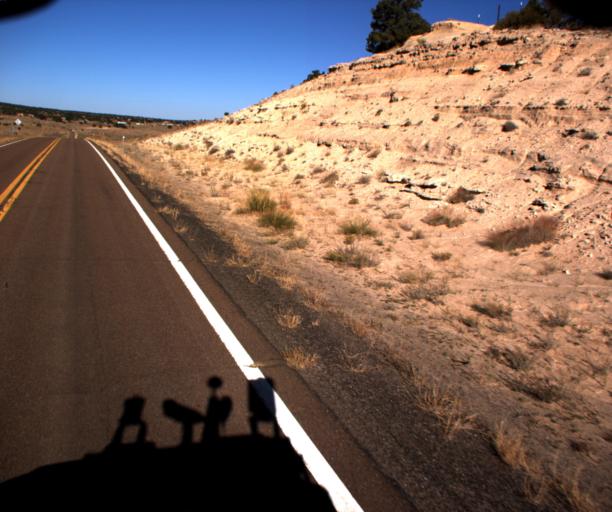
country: US
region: Arizona
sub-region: Navajo County
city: First Mesa
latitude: 35.7631
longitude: -109.9753
